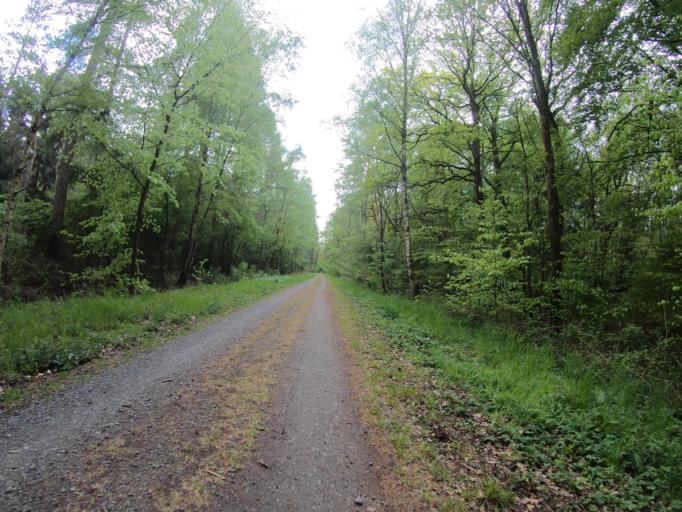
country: DE
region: Lower Saxony
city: Gifhorn
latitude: 52.4989
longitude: 10.5646
